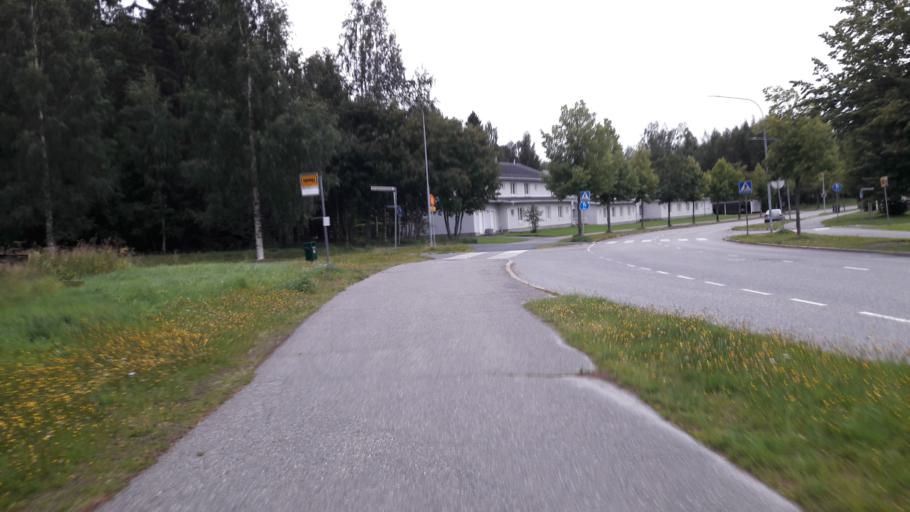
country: FI
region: North Karelia
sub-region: Joensuu
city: Joensuu
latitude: 62.6176
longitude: 29.6950
